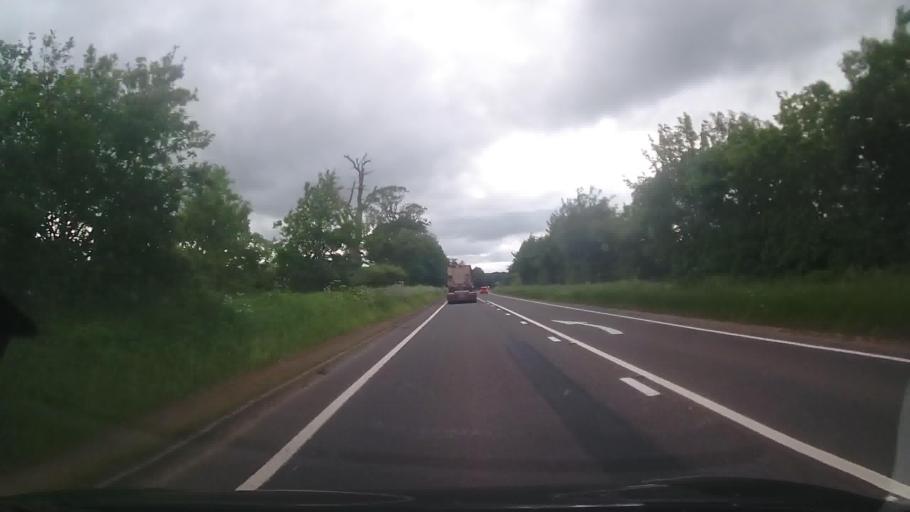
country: GB
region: England
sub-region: Telford and Wrekin
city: Chetwynd
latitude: 52.7919
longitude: -2.4066
